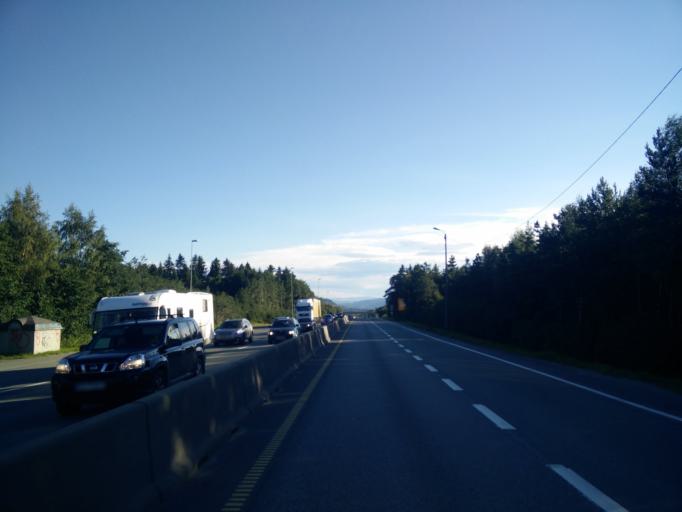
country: NO
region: Sor-Trondelag
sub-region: Trondheim
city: Trondheim
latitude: 63.3383
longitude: 10.3615
